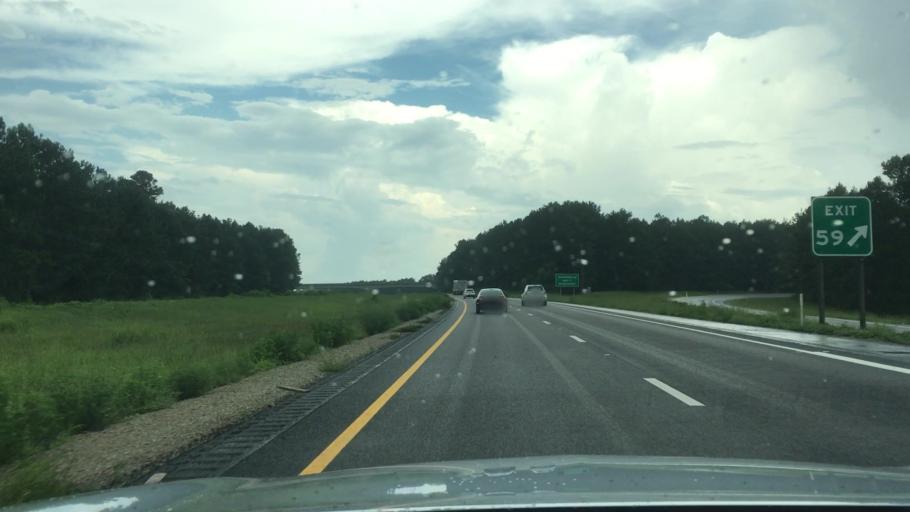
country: US
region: Mississippi
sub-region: Forrest County
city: Hattiesburg
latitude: 31.2355
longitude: -89.3224
